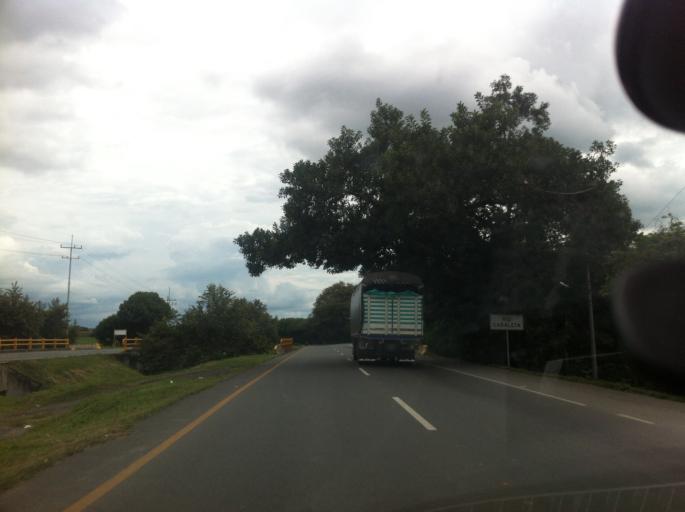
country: CO
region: Valle del Cauca
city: El Cerrito
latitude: 3.7079
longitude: -76.3197
